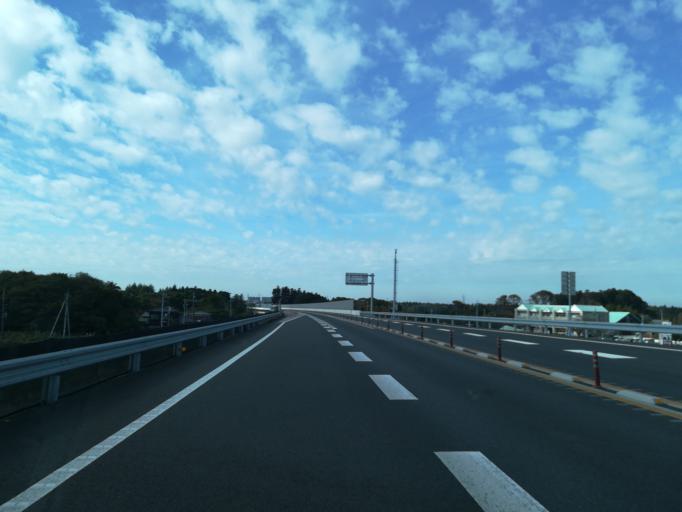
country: JP
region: Ibaraki
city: Naka
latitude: 36.0577
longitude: 140.0855
